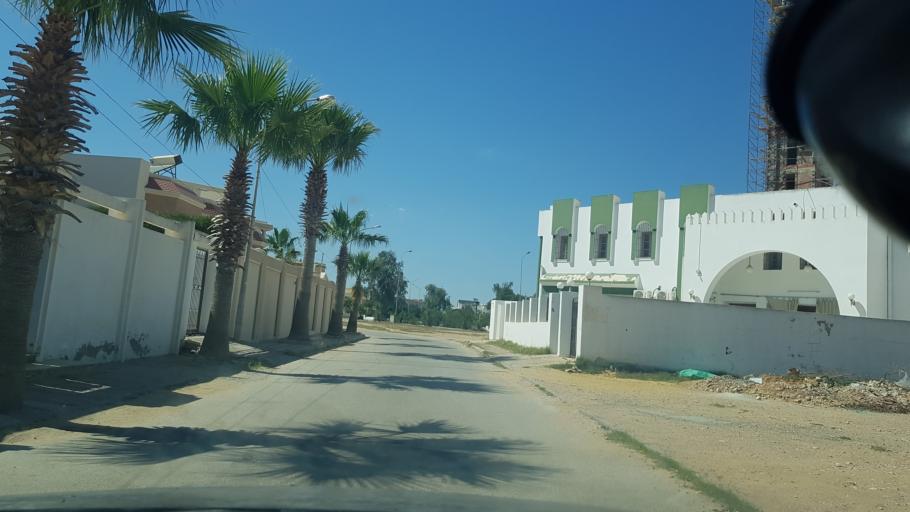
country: TN
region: Safaqis
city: Al Qarmadah
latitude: 34.8261
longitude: 10.7591
